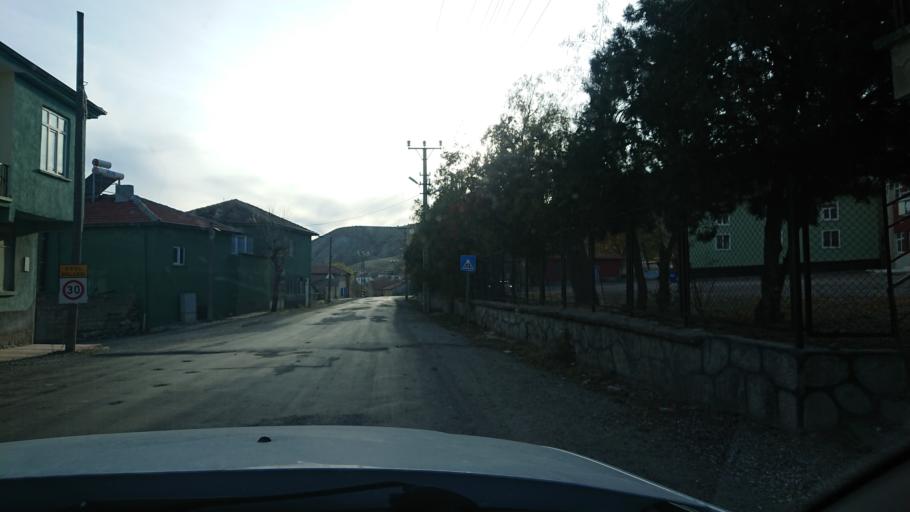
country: TR
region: Ankara
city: Sereflikochisar
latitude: 38.7667
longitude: 33.7005
